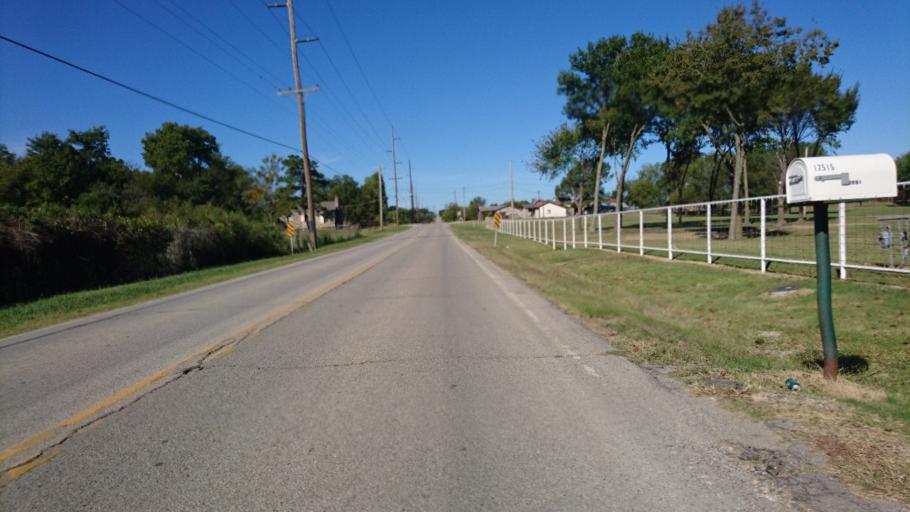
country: US
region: Oklahoma
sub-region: Rogers County
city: Catoosa
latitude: 36.1480
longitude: -95.7808
